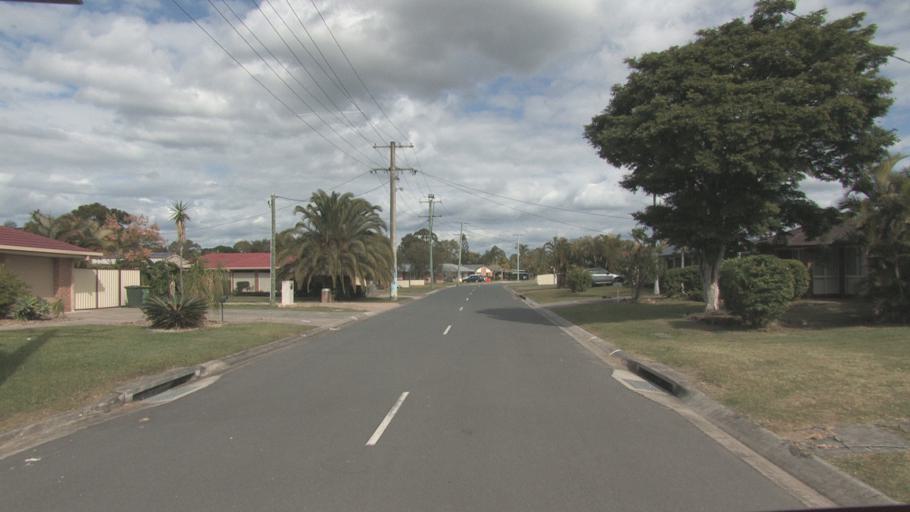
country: AU
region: Queensland
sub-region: Logan
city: Windaroo
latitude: -27.7368
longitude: 153.2102
